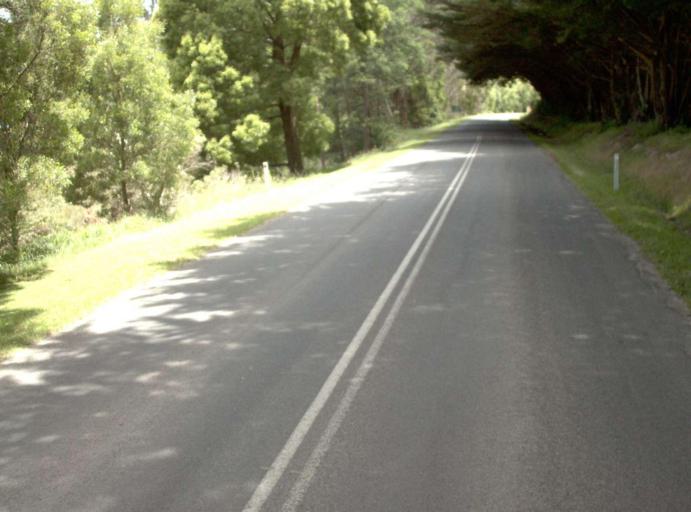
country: AU
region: Victoria
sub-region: Bass Coast
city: North Wonthaggi
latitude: -38.6976
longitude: 146.0875
